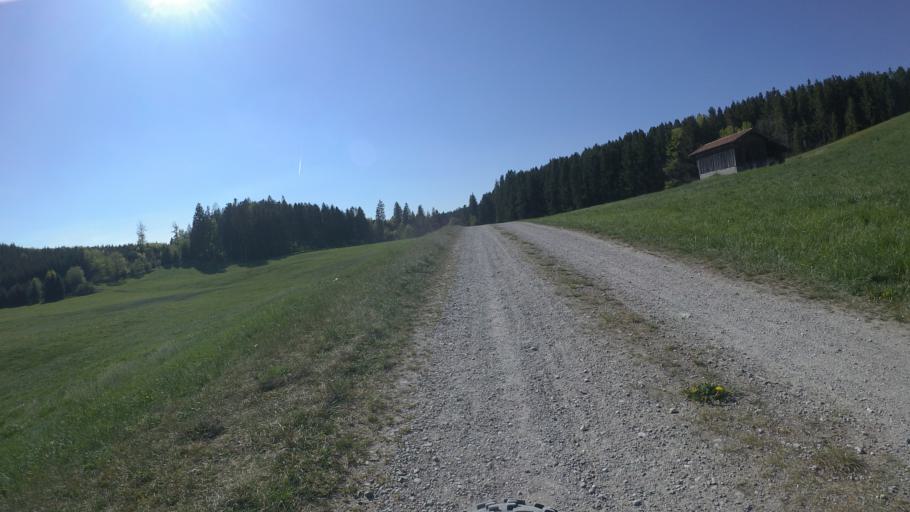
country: DE
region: Bavaria
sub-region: Upper Bavaria
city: Chieming
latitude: 47.9441
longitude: 12.5416
